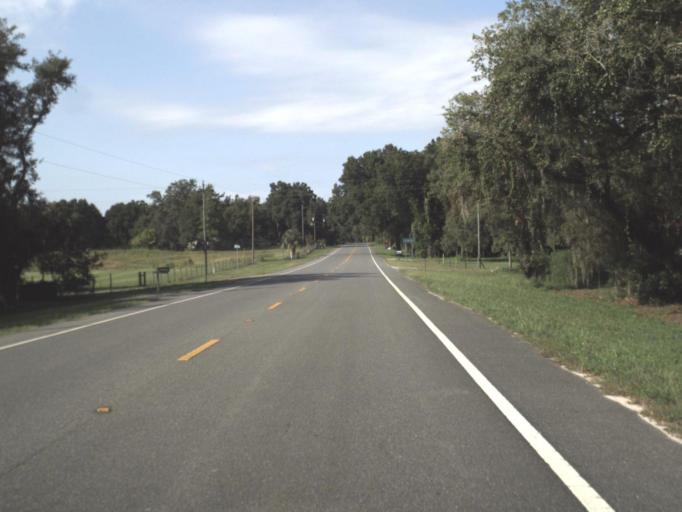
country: US
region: Florida
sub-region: Pasco County
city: Lacoochee
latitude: 28.4743
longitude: -82.1567
